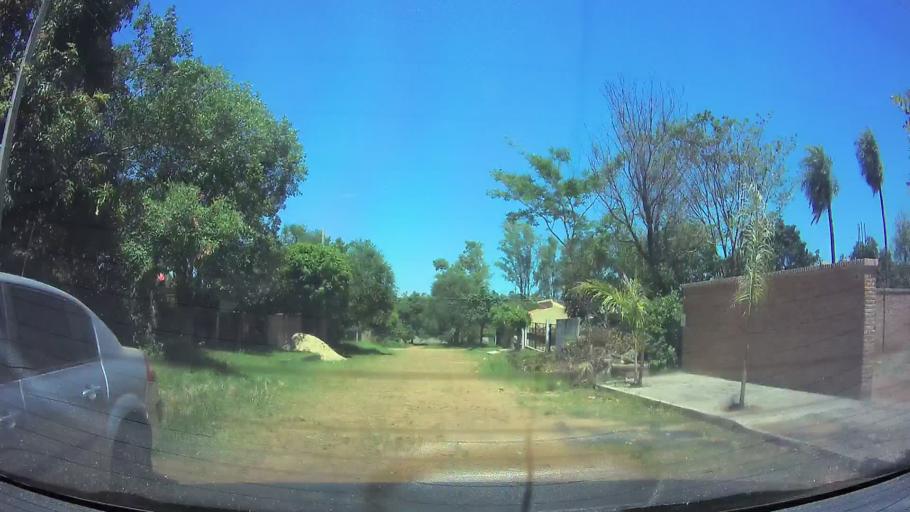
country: PY
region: Central
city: Limpio
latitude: -25.2420
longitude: -57.4869
